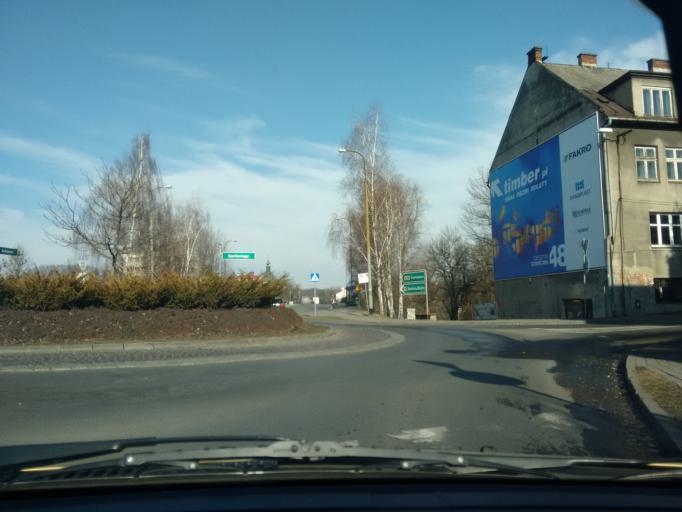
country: PL
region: Silesian Voivodeship
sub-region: Powiat cieszynski
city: Cieszyn
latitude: 49.7494
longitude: 18.6404
